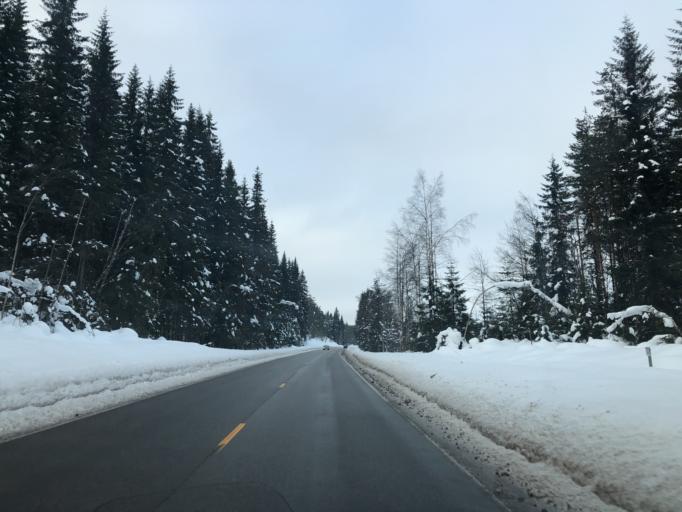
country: NO
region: Hedmark
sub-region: Trysil
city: Innbygda
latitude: 61.2760
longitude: 12.2892
